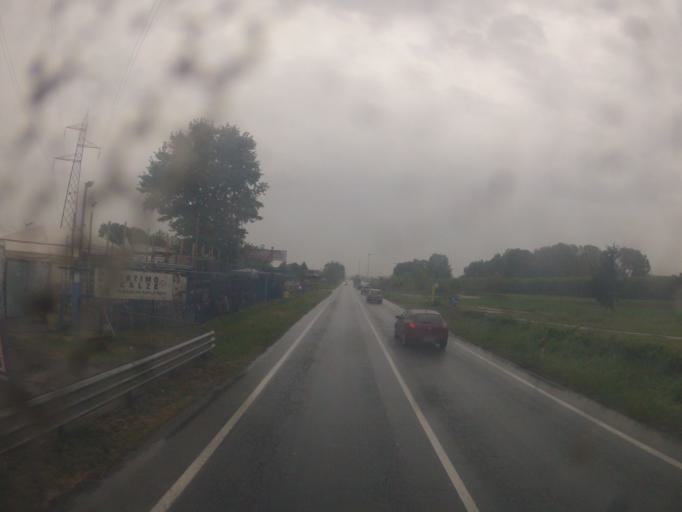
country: IT
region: Piedmont
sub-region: Provincia di Torino
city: La Loggia
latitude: 44.9361
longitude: 7.6713
